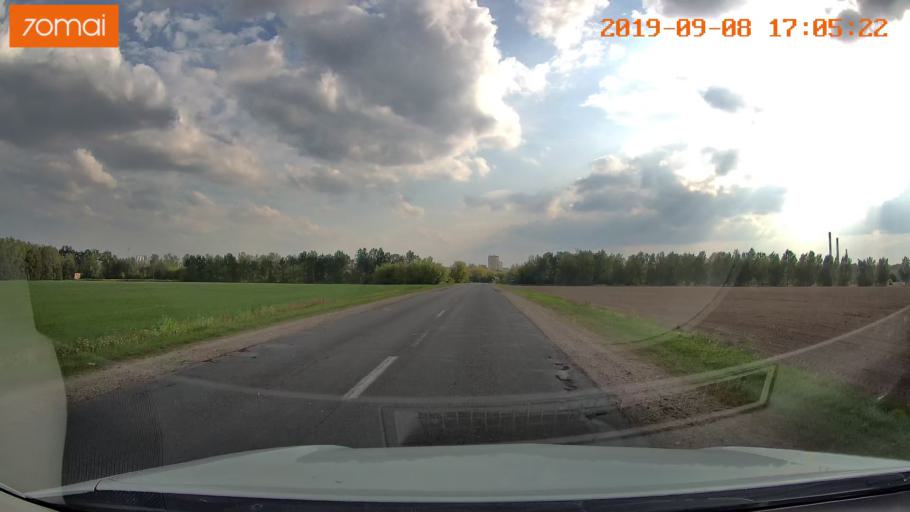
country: BY
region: Grodnenskaya
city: Hrodna
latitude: 53.6785
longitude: 23.9547
